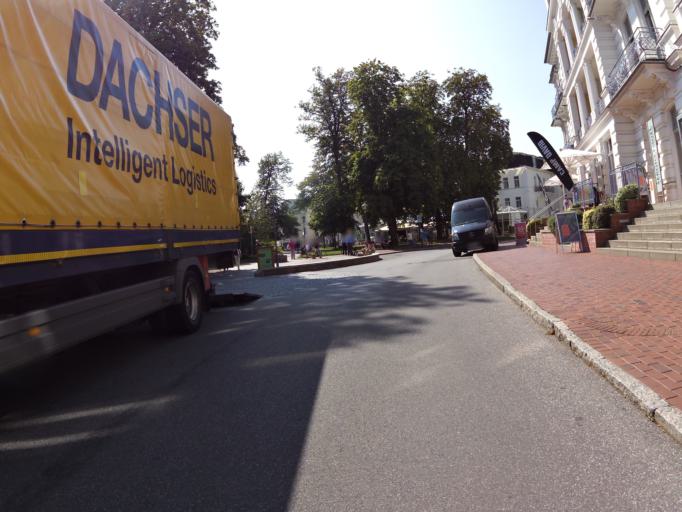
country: DE
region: Mecklenburg-Vorpommern
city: Seebad Heringsdorf
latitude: 53.9569
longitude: 14.1668
